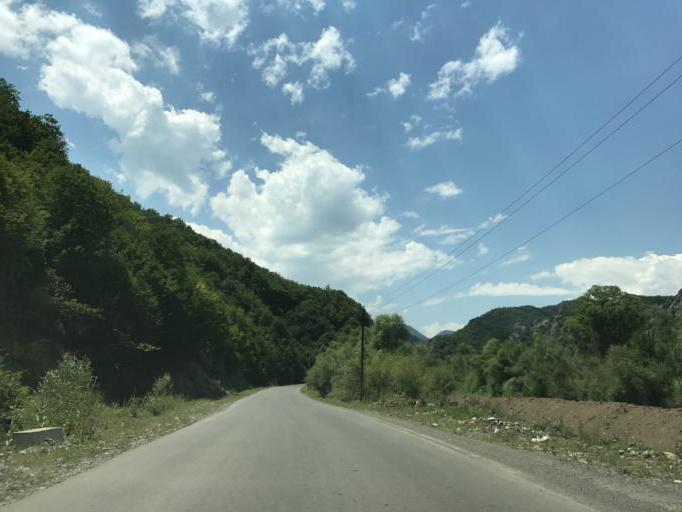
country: AZ
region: Kalbacar Rayonu
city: Kerbakhiar
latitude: 40.2284
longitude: 46.1513
